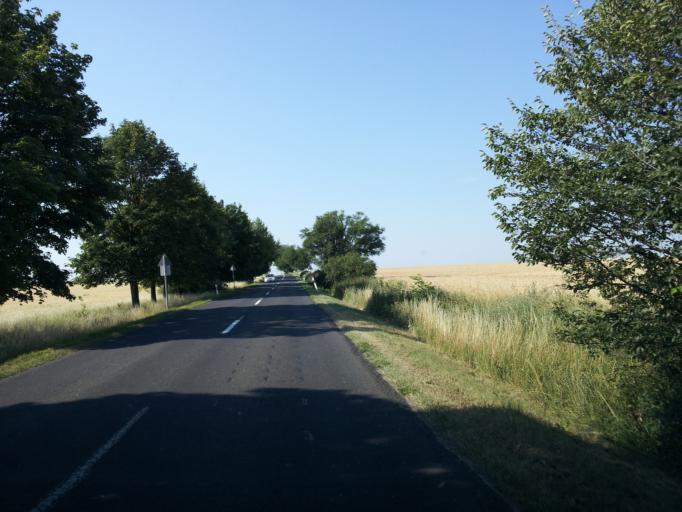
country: HU
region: Fejer
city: Lovasbereny
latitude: 47.4023
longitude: 18.5859
